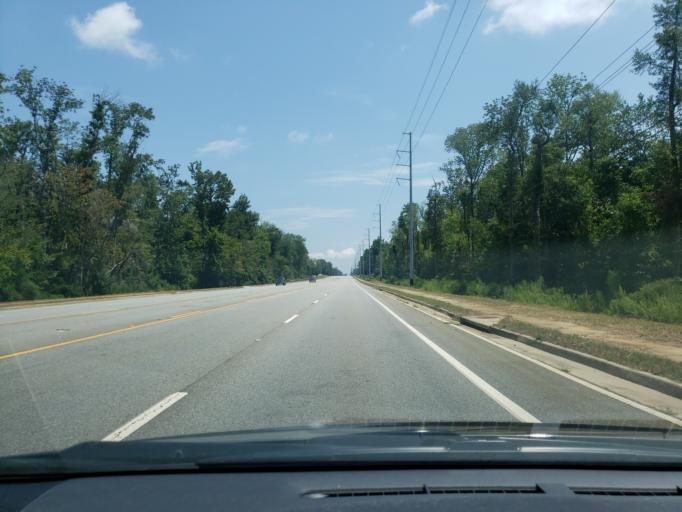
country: US
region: Georgia
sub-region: Dougherty County
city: Albany
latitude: 31.5856
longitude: -84.2676
